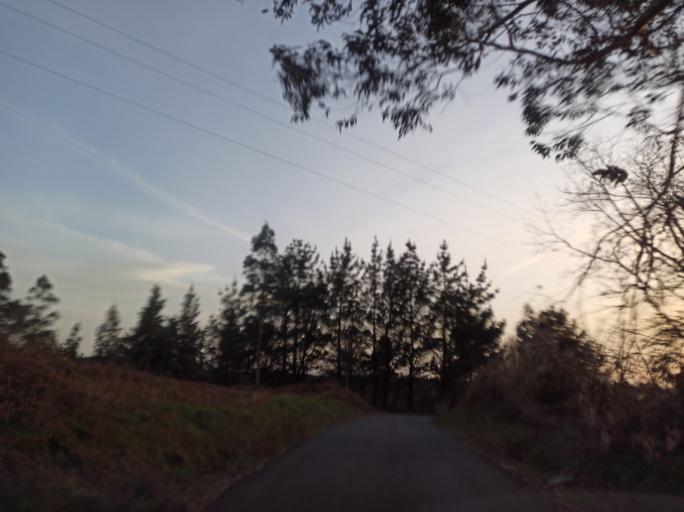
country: ES
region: Galicia
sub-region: Provincia da Coruna
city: Coiros
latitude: 43.1855
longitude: -8.1288
